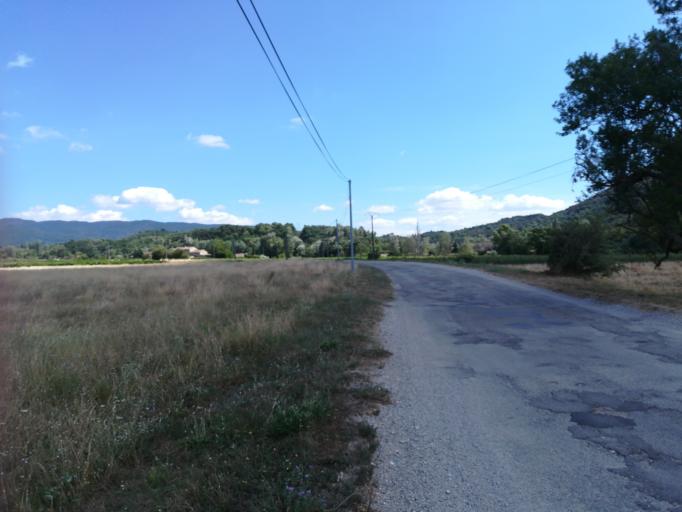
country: FR
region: Provence-Alpes-Cote d'Azur
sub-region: Departement du Vaucluse
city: Vaison-la-Romaine
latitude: 44.2103
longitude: 5.1075
